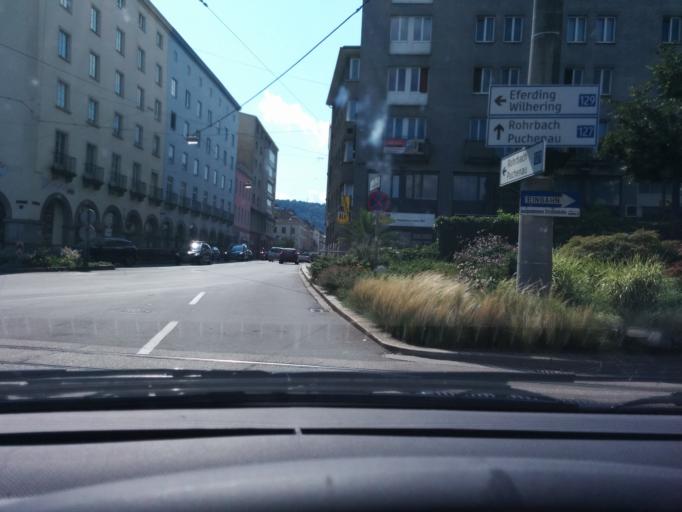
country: AT
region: Upper Austria
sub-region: Linz Stadt
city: Linz
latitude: 48.3114
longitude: 14.2828
